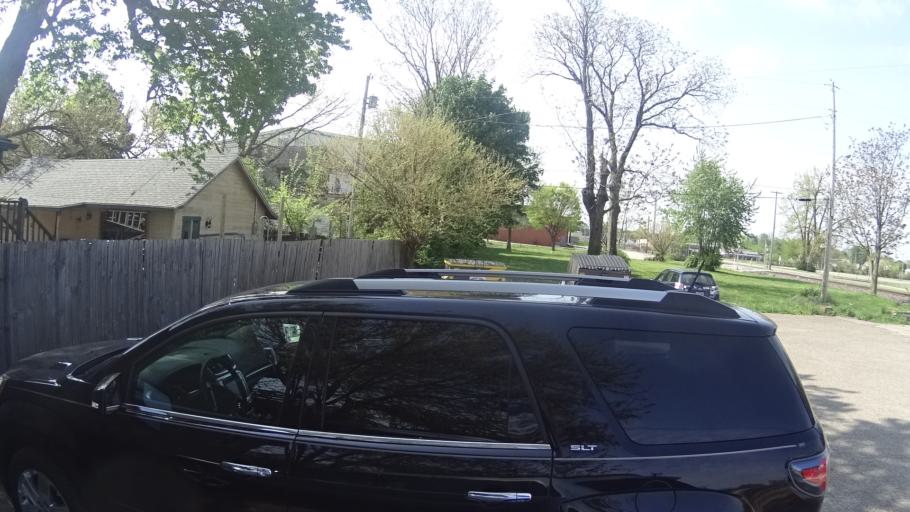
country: US
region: Indiana
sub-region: Madison County
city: Anderson
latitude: 40.1048
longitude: -85.6868
